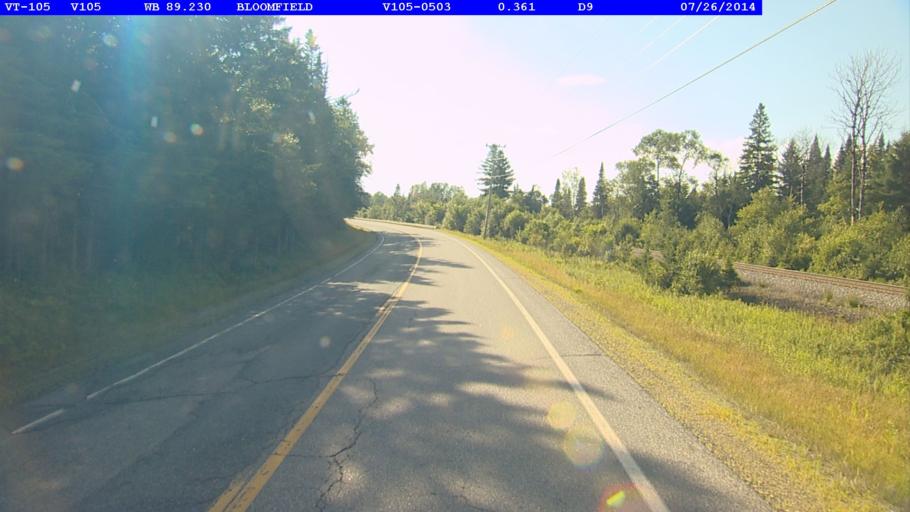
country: US
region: New Hampshire
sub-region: Coos County
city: Stratford
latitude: 44.7802
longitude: -71.6837
